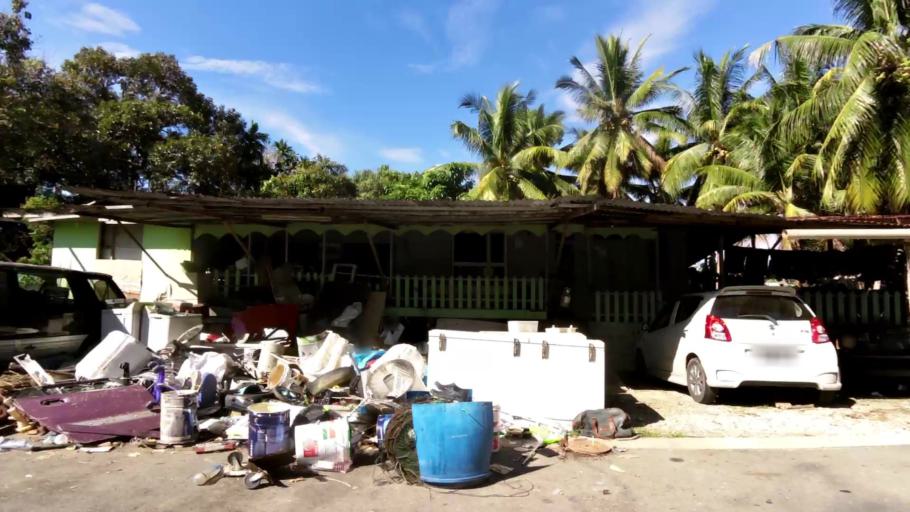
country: BN
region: Brunei and Muara
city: Bandar Seri Begawan
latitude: 4.9656
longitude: 114.9274
